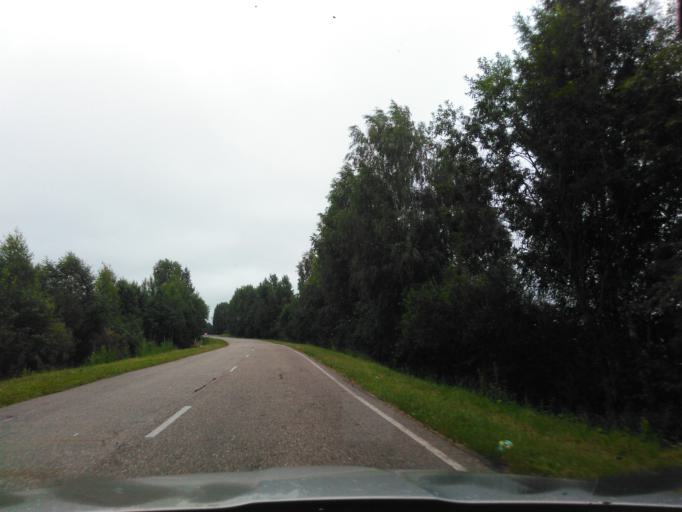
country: RU
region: Tverskaya
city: Zavidovo
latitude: 56.6050
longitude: 36.6391
